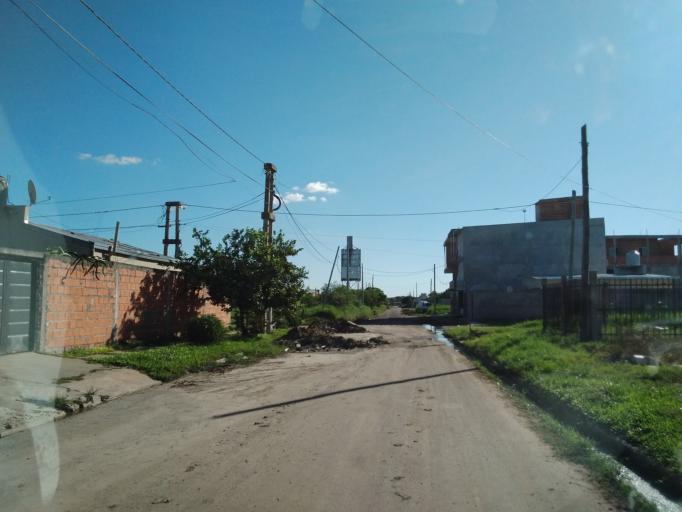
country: AR
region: Corrientes
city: Corrientes
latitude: -27.4564
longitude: -58.7699
